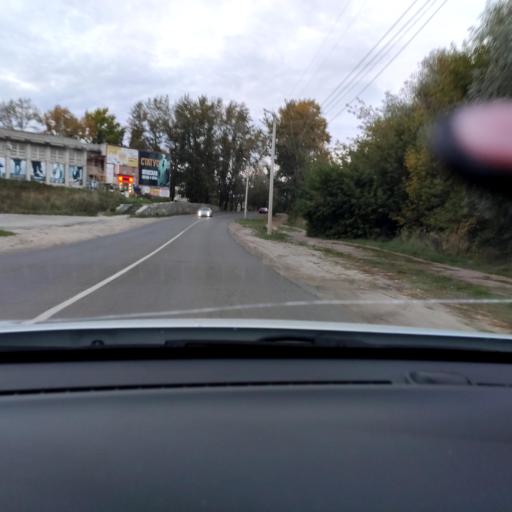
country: RU
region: Mariy-El
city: Volzhsk
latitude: 55.8500
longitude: 48.3877
